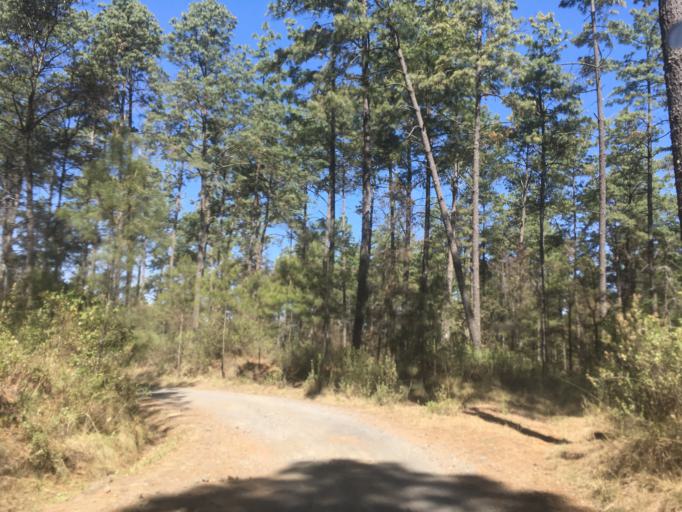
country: MX
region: Michoacan
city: Angahuan
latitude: 19.4931
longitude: -102.2003
